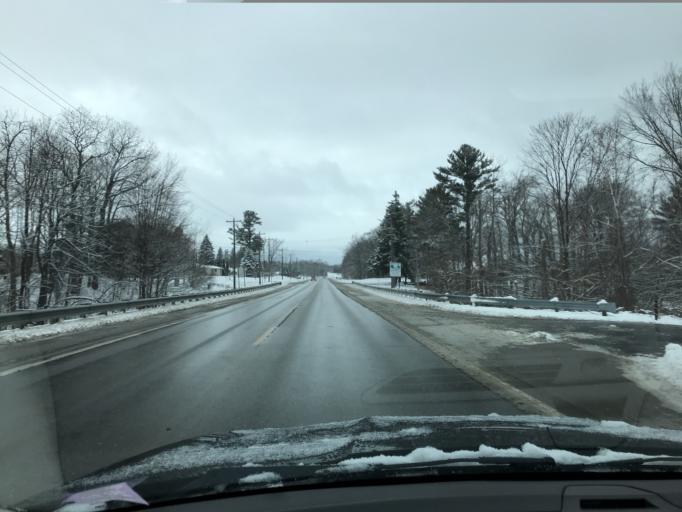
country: US
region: Michigan
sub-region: Charlevoix County
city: Charlevoix
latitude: 45.2796
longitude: -85.2316
